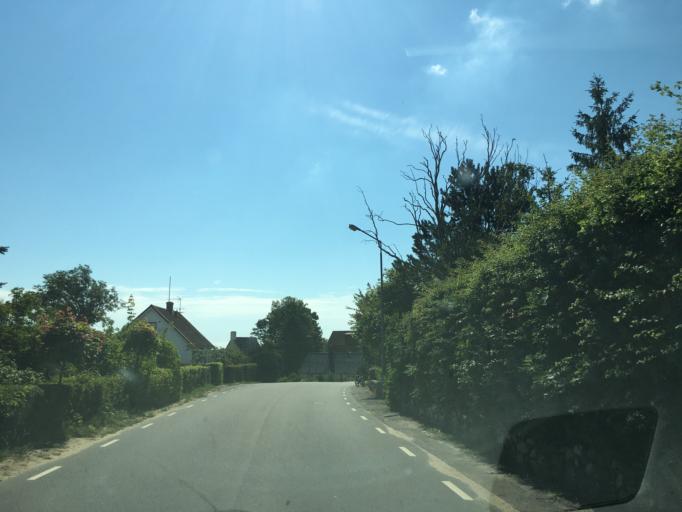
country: SE
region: Skane
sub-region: Simrishamns Kommun
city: Simrishamn
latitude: 55.5939
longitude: 14.3113
